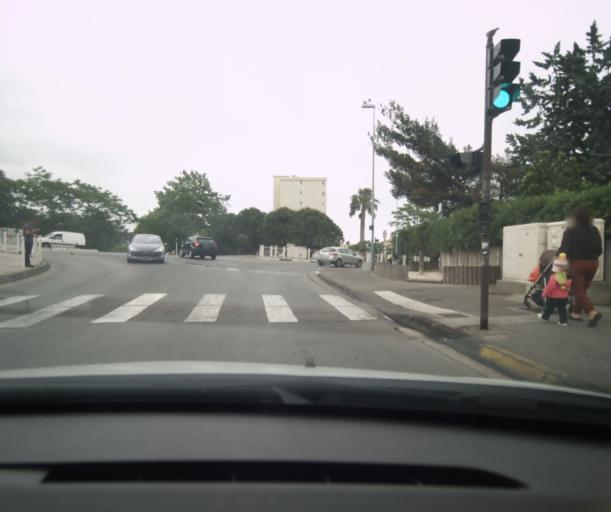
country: FR
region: Provence-Alpes-Cote d'Azur
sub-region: Departement du Var
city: Toulon
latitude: 43.1252
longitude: 5.9457
